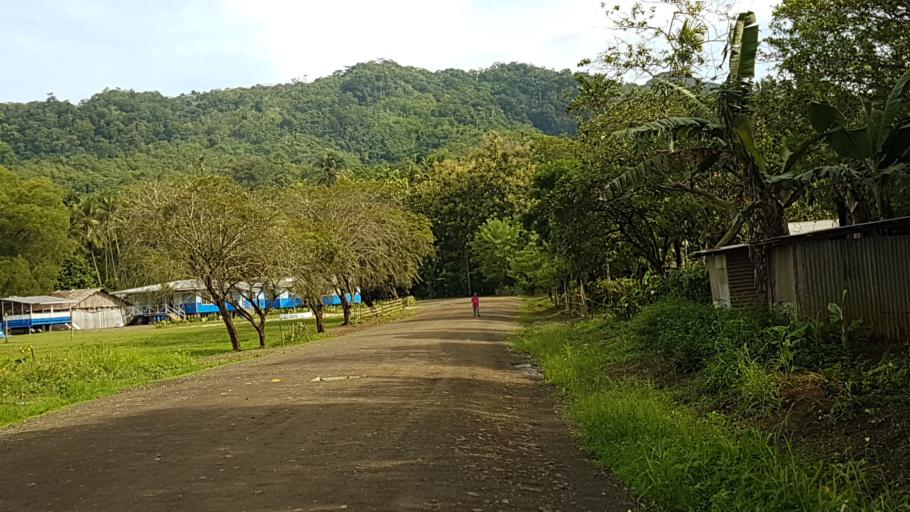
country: PG
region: Milne Bay
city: Alotau
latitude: -10.3211
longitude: 150.6814
